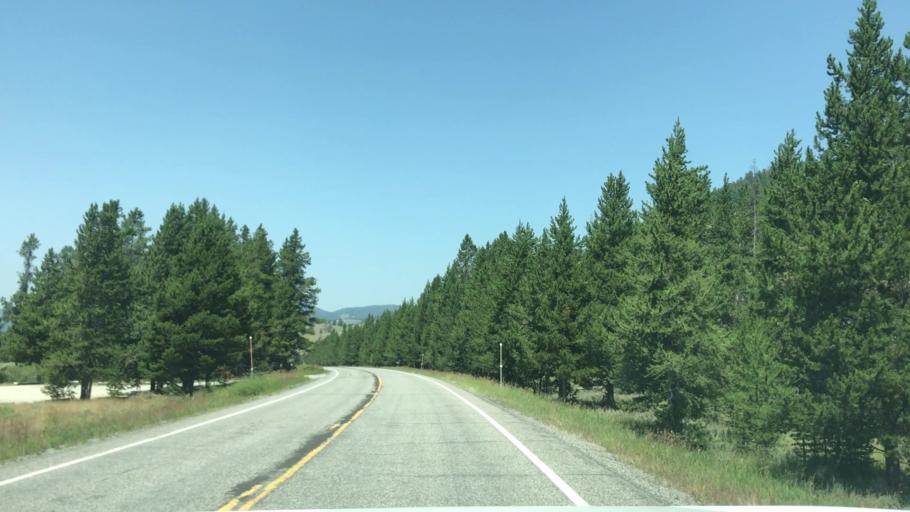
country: US
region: Montana
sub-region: Gallatin County
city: Big Sky
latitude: 45.0337
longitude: -111.1128
